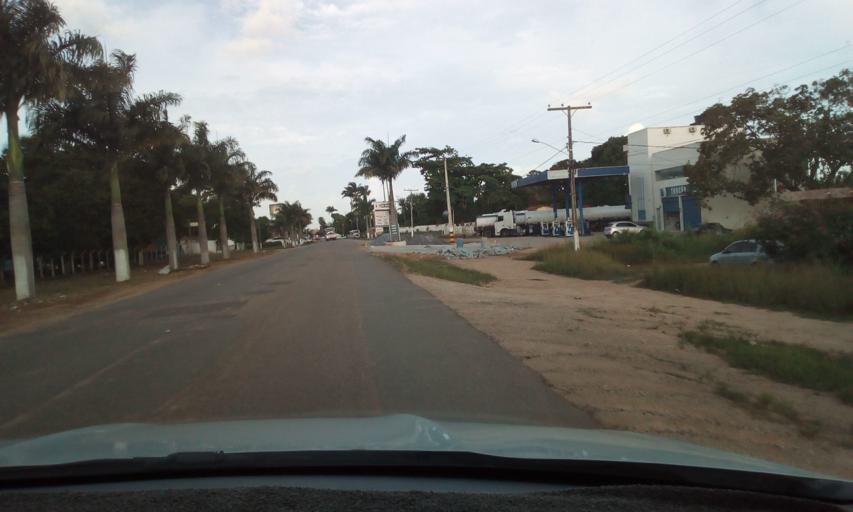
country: BR
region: Pernambuco
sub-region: Gloria Do Goita
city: Gloria do Goita
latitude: -7.9980
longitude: -35.2184
